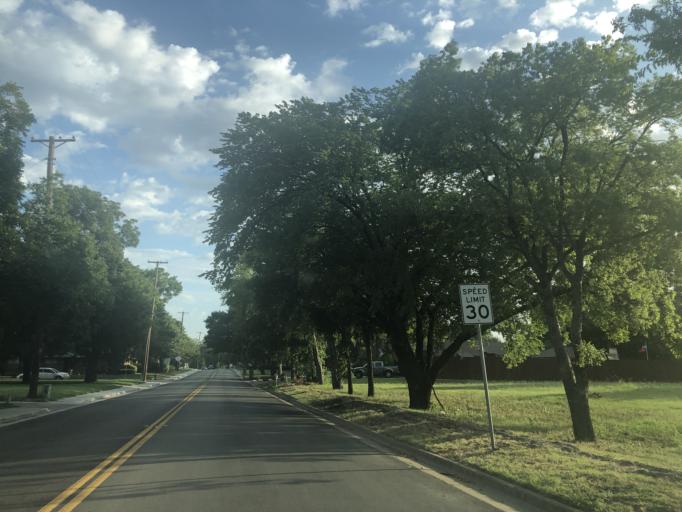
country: US
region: Texas
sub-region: Dallas County
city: Grand Prairie
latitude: 32.7609
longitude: -97.0124
